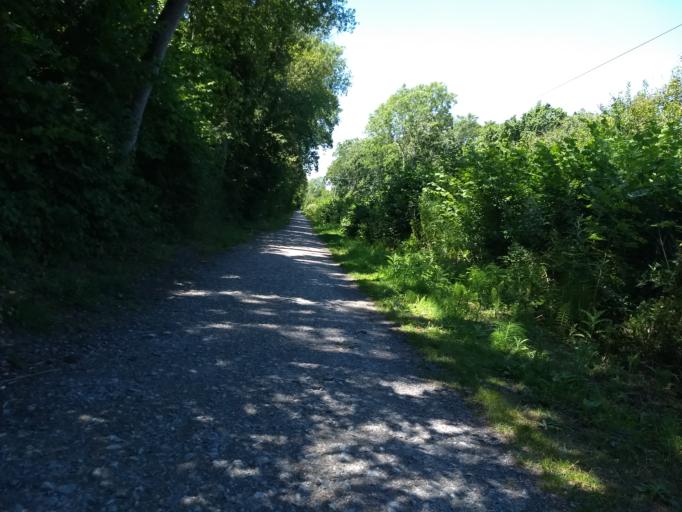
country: GB
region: England
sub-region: Isle of Wight
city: Newport
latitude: 50.7205
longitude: -1.2555
